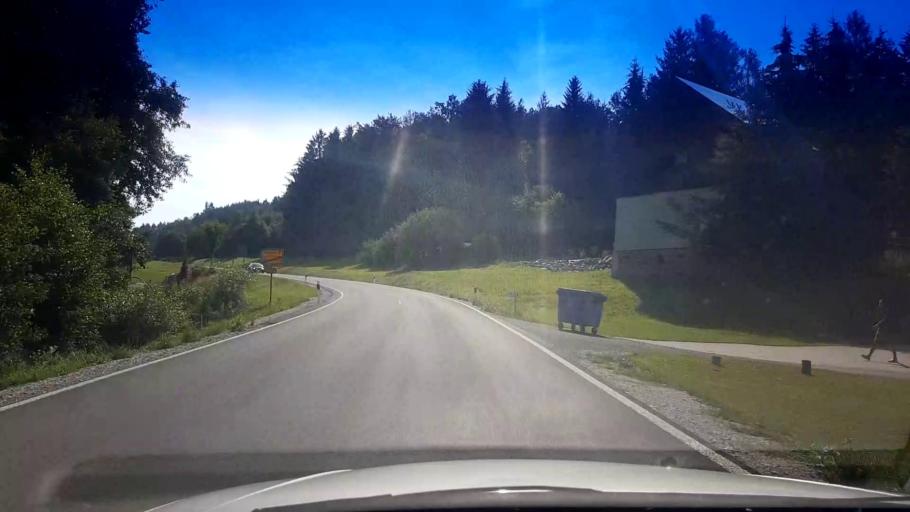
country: DE
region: Bavaria
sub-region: Upper Franconia
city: Plankenfels
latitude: 49.9355
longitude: 11.3551
